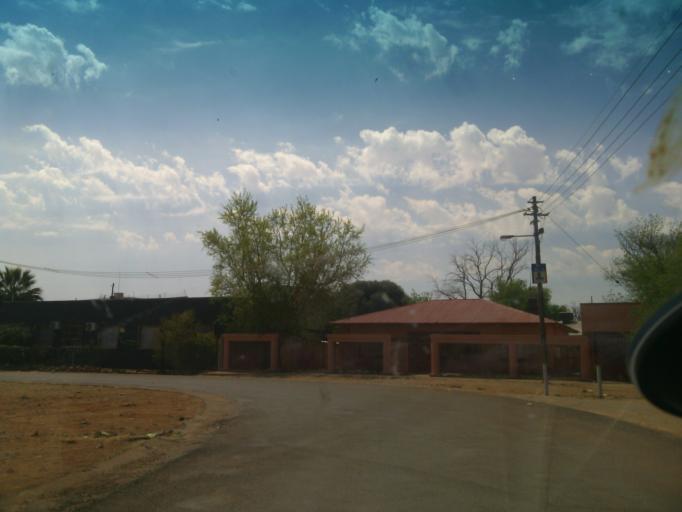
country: ZA
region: Northern Cape
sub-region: Frances Baard District Municipality
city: Barkly West
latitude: -28.5395
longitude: 24.5179
